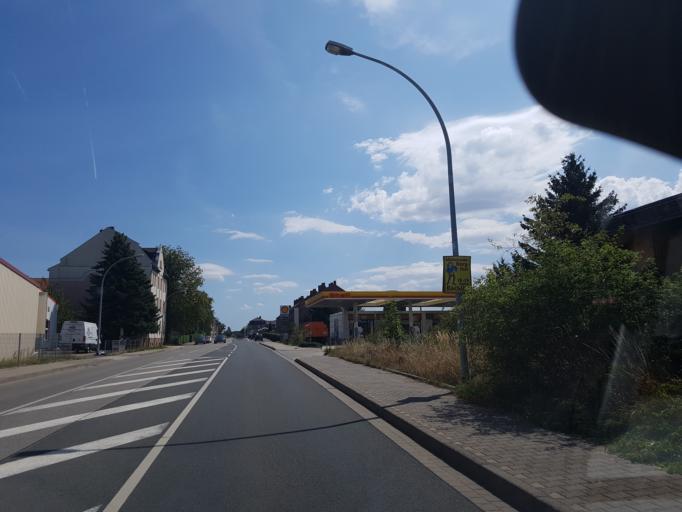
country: DE
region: Saxony
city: Waldheim
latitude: 51.0786
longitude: 13.0021
